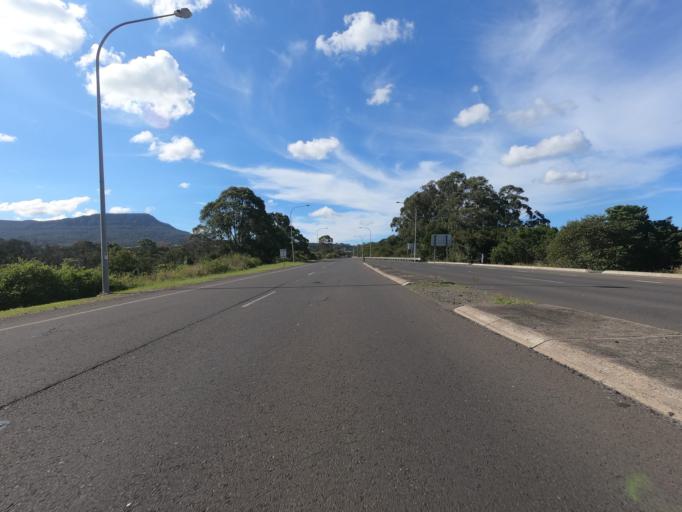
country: AU
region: New South Wales
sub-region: Wollongong
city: Koonawarra
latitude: -34.4826
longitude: 150.8026
